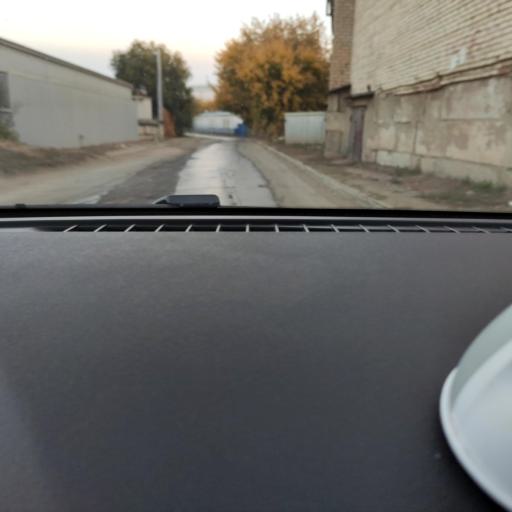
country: RU
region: Samara
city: Samara
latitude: 53.1832
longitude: 50.1437
